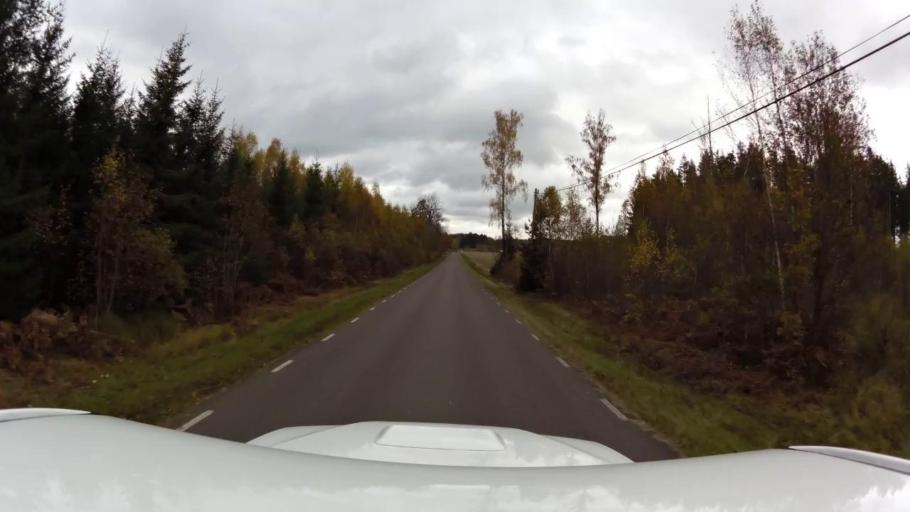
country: SE
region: OEstergoetland
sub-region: Motala Kommun
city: Borensberg
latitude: 58.5632
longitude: 15.3904
